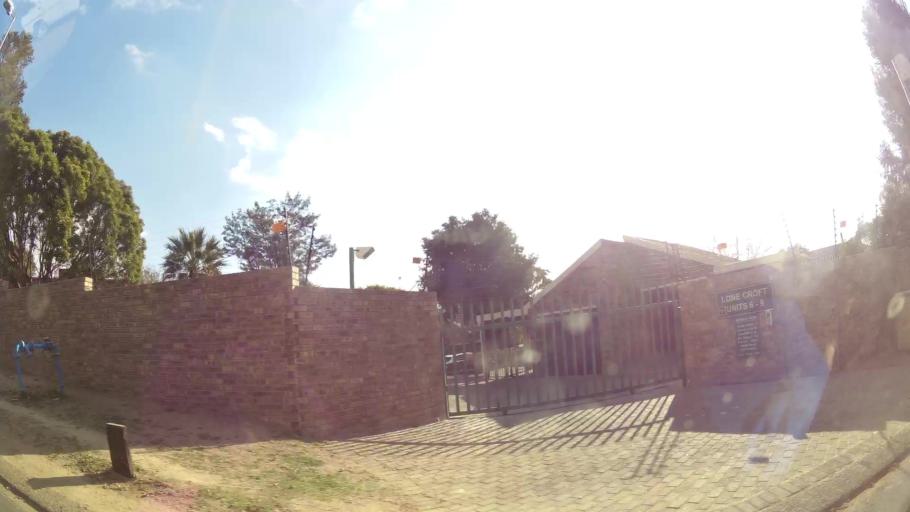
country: ZA
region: Gauteng
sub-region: City of Johannesburg Metropolitan Municipality
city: Diepsloot
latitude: -26.0152
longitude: 28.0316
